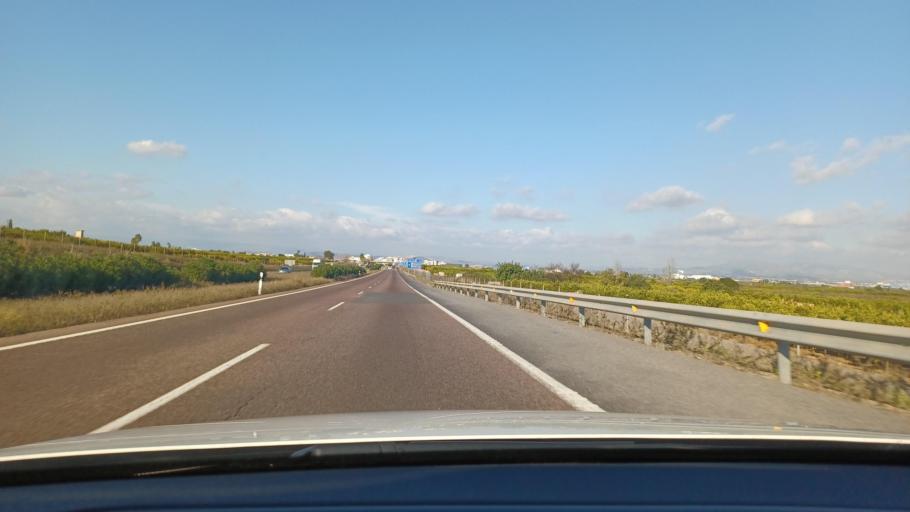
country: ES
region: Valencia
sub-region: Provincia de Castello
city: Betxi
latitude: 39.9098
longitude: -0.1953
